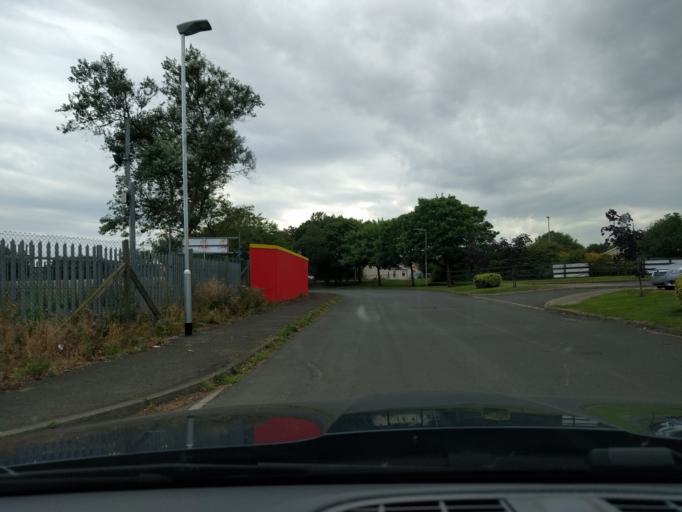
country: GB
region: England
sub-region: Northumberland
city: Amble
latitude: 55.3286
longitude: -1.5848
